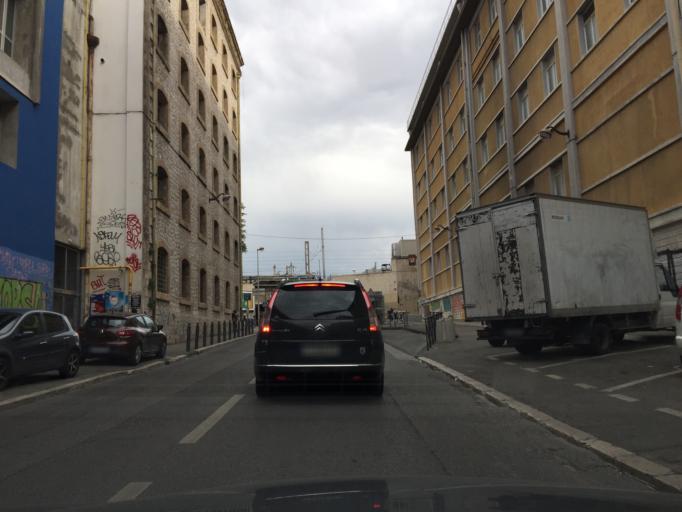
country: FR
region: Provence-Alpes-Cote d'Azur
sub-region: Departement des Bouches-du-Rhone
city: Marseille 01
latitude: 43.3100
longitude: 5.3899
